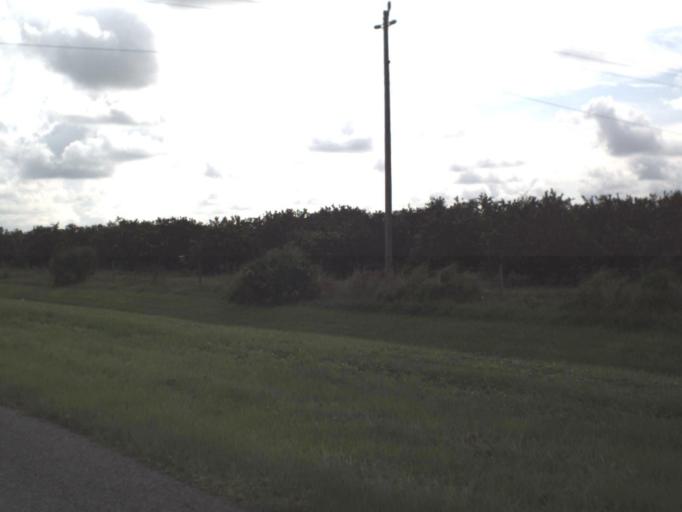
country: US
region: Florida
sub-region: Lee County
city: Alva
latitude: 26.7090
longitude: -81.5874
